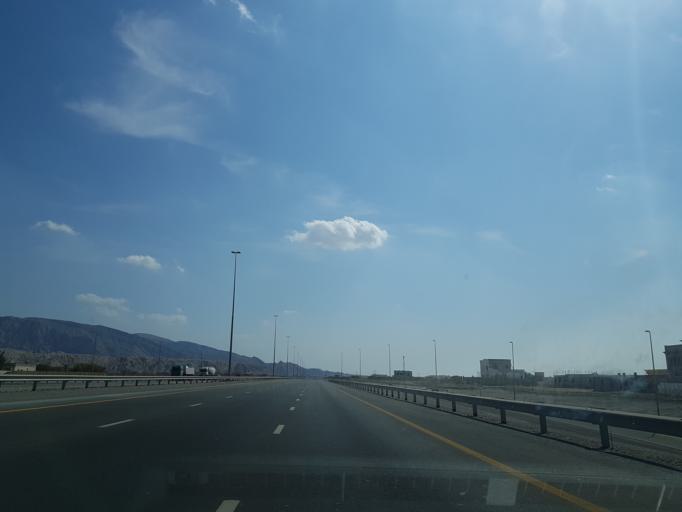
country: AE
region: Ra's al Khaymah
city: Ras al-Khaimah
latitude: 25.7975
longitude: 56.0306
